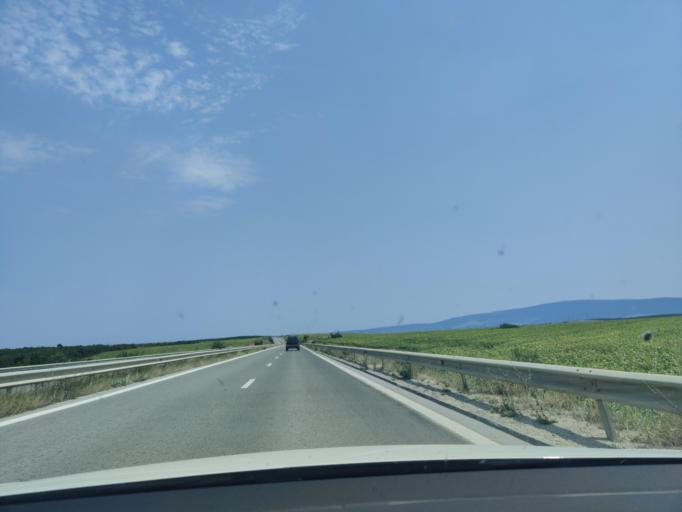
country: BG
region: Montana
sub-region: Obshtina Montana
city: Montana
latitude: 43.4290
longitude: 23.1775
